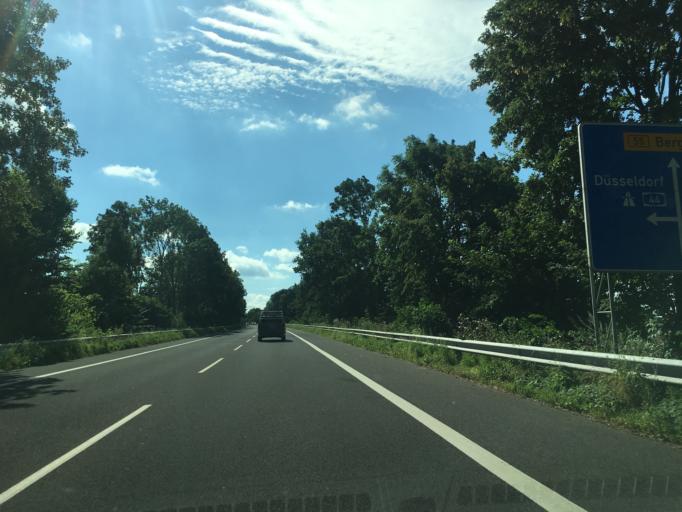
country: DE
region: North Rhine-Westphalia
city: Julich
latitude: 50.9677
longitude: 6.3600
